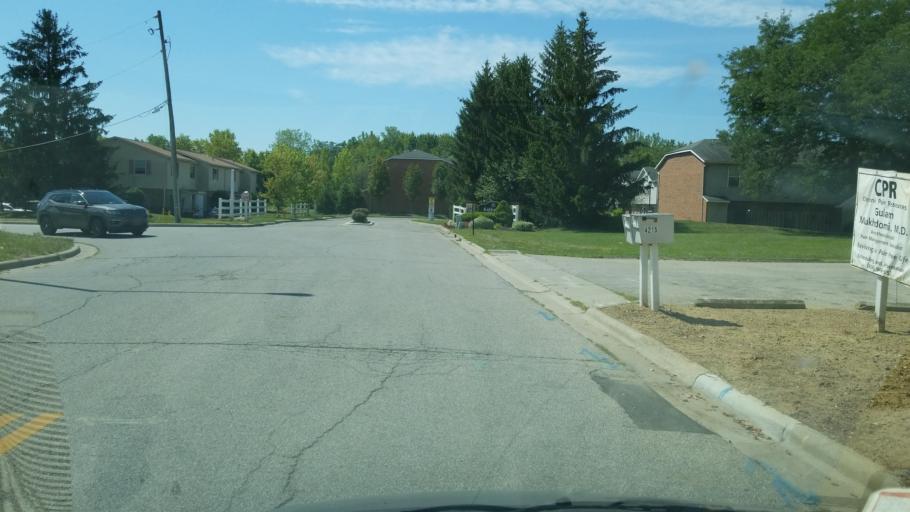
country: US
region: Ohio
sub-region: Franklin County
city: Grove City
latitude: 39.8765
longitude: -83.0559
